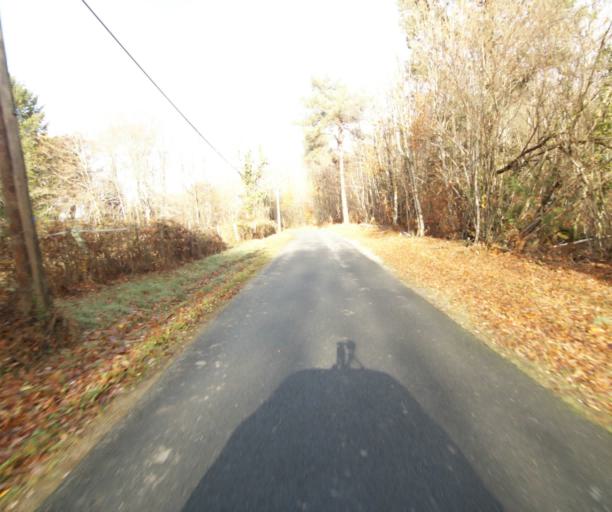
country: FR
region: Limousin
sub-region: Departement de la Correze
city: Sainte-Fortunade
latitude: 45.2183
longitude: 1.7500
